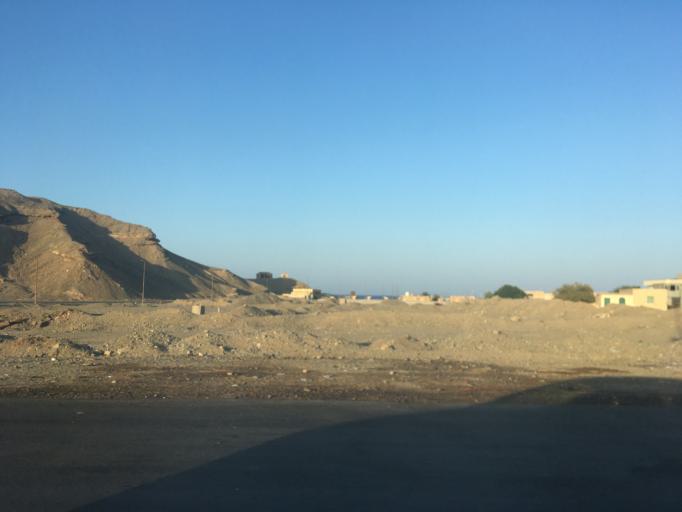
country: EG
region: Red Sea
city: Marsa Alam
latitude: 25.0702
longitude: 34.8897
